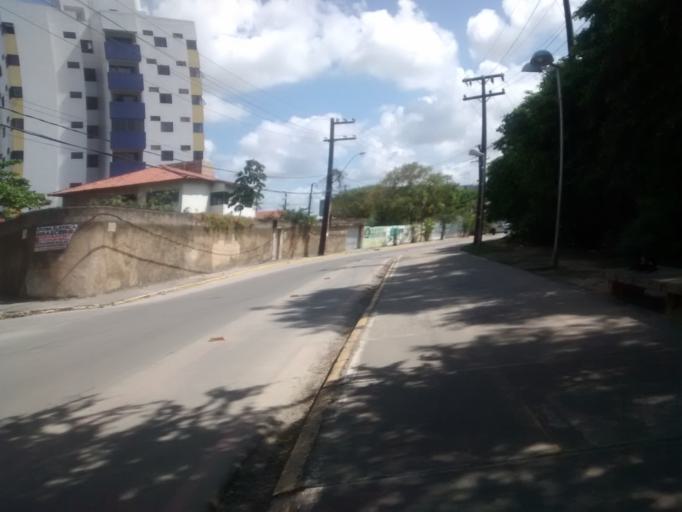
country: BR
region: Pernambuco
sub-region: Recife
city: Recife
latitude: -8.0962
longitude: -34.9140
